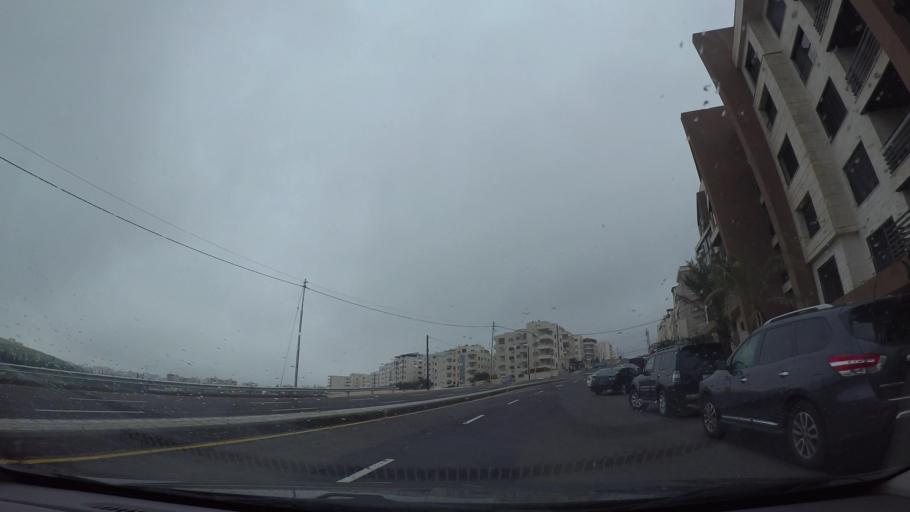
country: JO
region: Amman
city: Wadi as Sir
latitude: 31.9346
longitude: 35.8594
